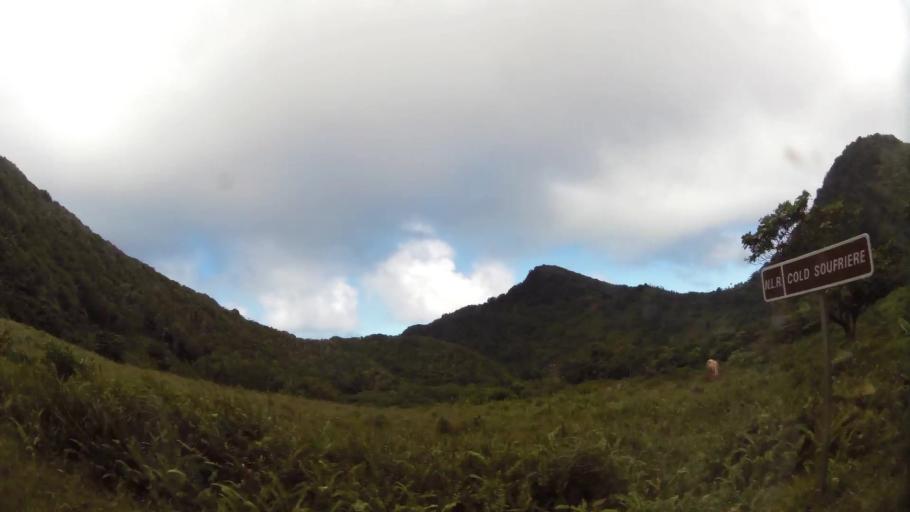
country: DM
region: Saint John
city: Portsmouth
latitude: 15.6174
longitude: -61.4398
